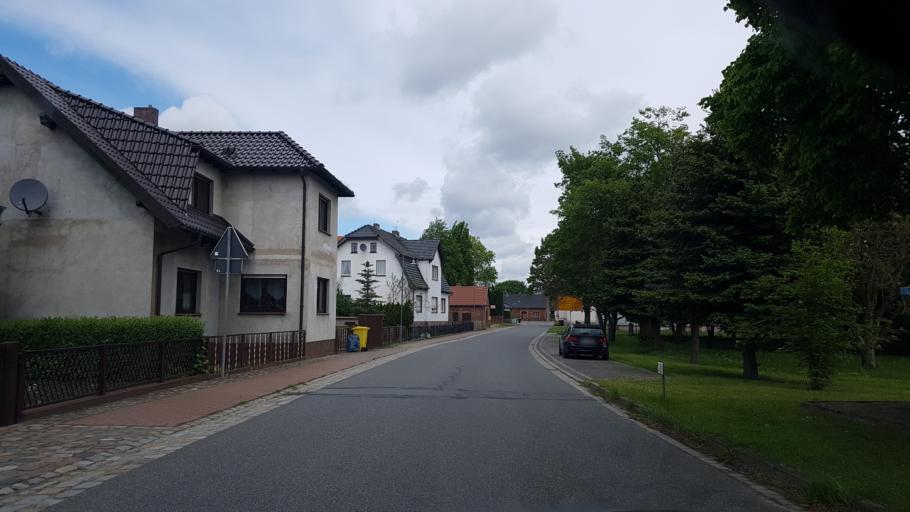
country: DE
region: Brandenburg
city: Neu Zauche
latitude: 51.9968
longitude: 14.0632
